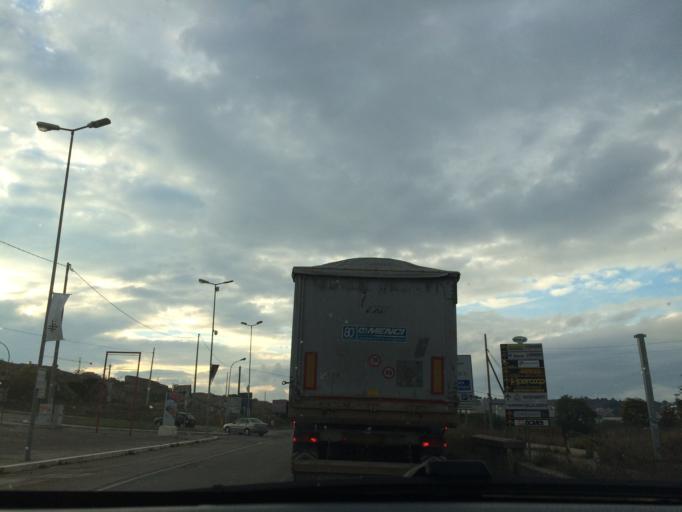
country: IT
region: Basilicate
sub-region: Provincia di Matera
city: Matera
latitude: 40.6815
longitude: 16.6028
